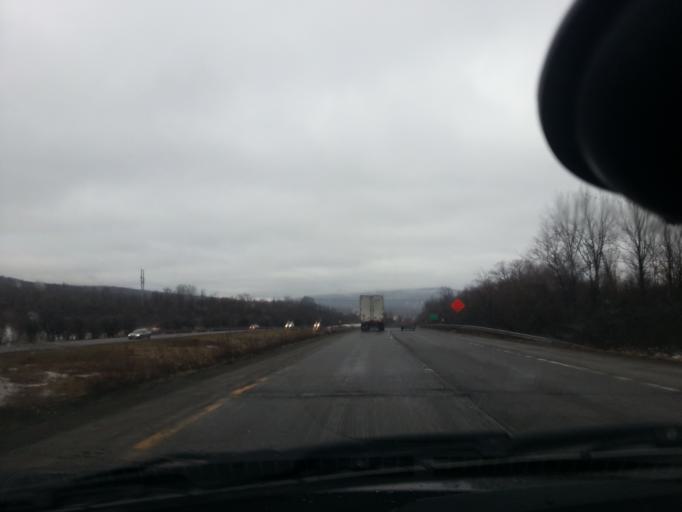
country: US
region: New York
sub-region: Onondaga County
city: Nedrow
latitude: 42.9760
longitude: -76.1321
